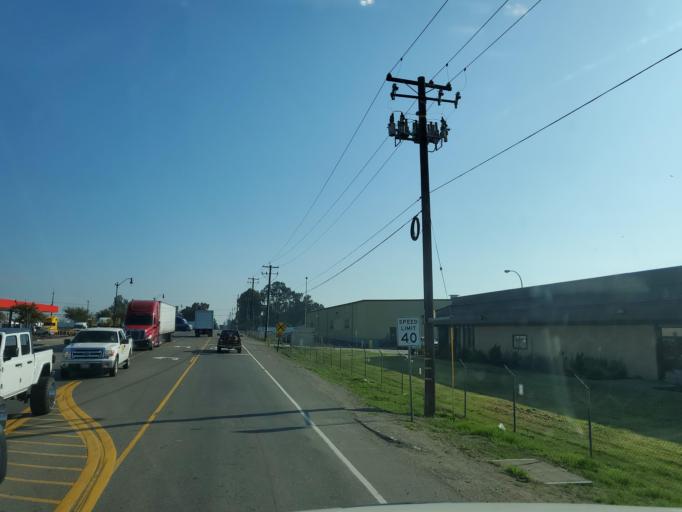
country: US
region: California
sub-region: San Joaquin County
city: French Camp
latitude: 37.8556
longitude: -121.2773
